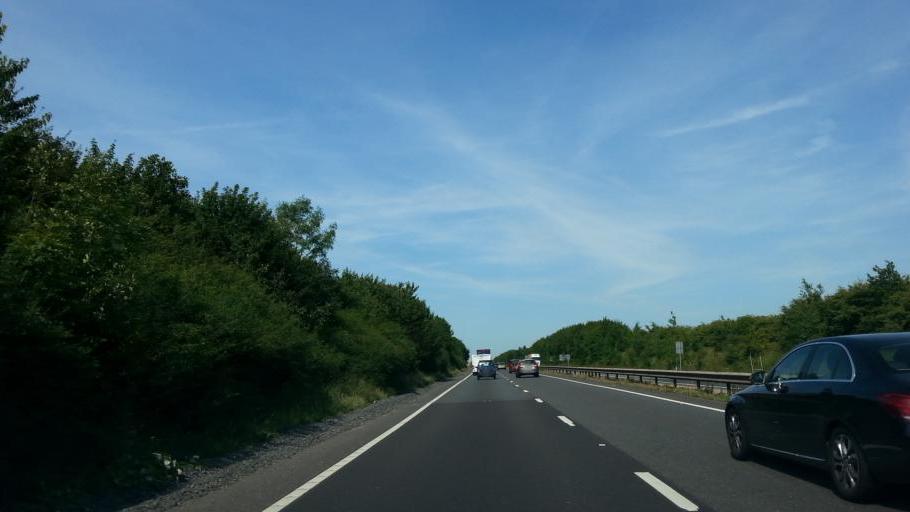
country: GB
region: England
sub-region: Leicestershire
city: Ashby de la Zouch
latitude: 52.7540
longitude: -1.4419
